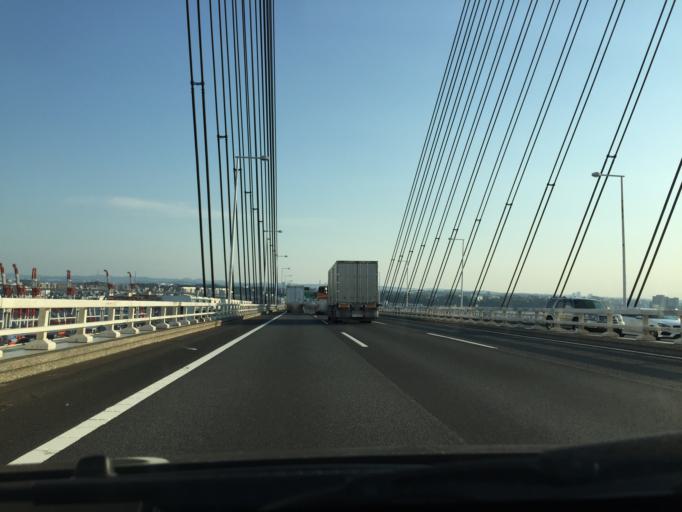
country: JP
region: Kanagawa
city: Yokohama
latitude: 35.4527
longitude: 139.6731
